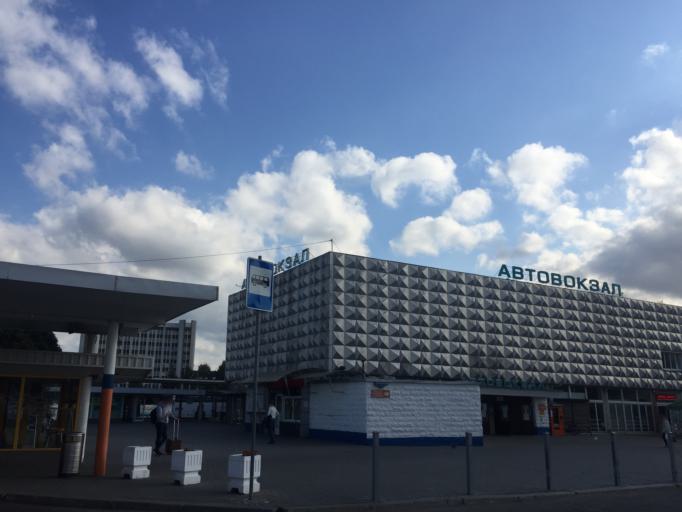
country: RU
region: Kaliningrad
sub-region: Gorod Kaliningrad
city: Kaliningrad
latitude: 54.6940
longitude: 20.5015
